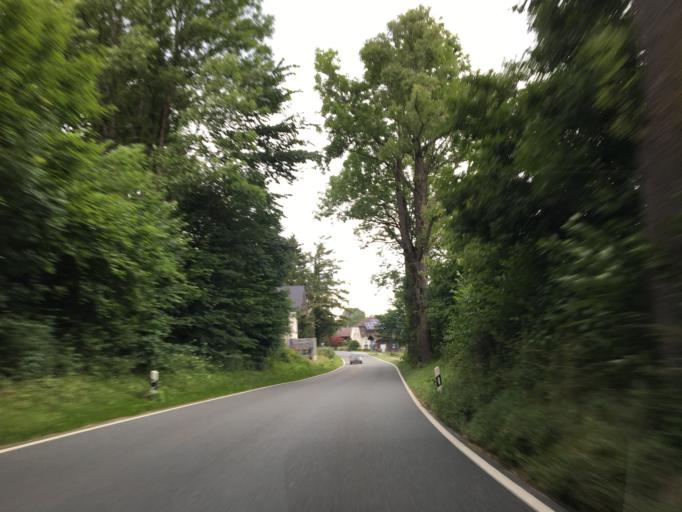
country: DE
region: Bavaria
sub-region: Upper Bavaria
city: Flintsbach
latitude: 47.7116
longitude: 12.1451
